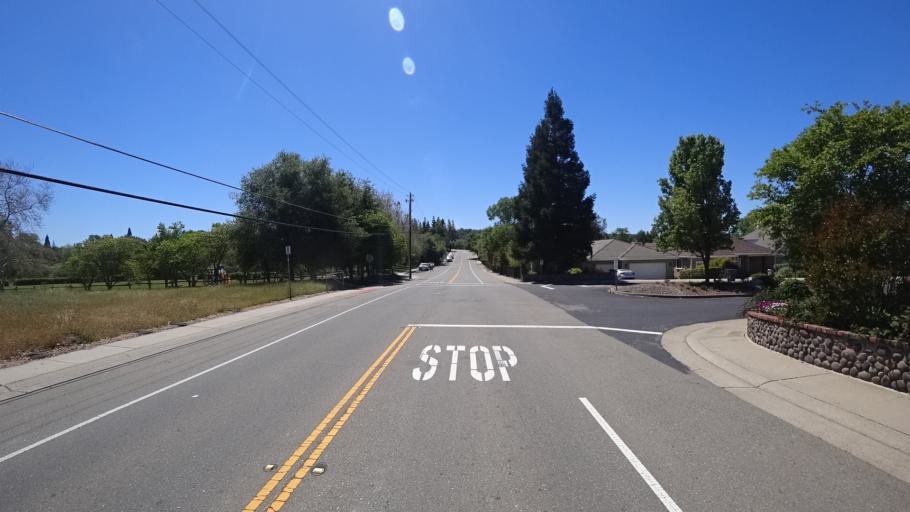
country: US
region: California
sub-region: Placer County
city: Rocklin
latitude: 38.7870
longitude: -121.2151
